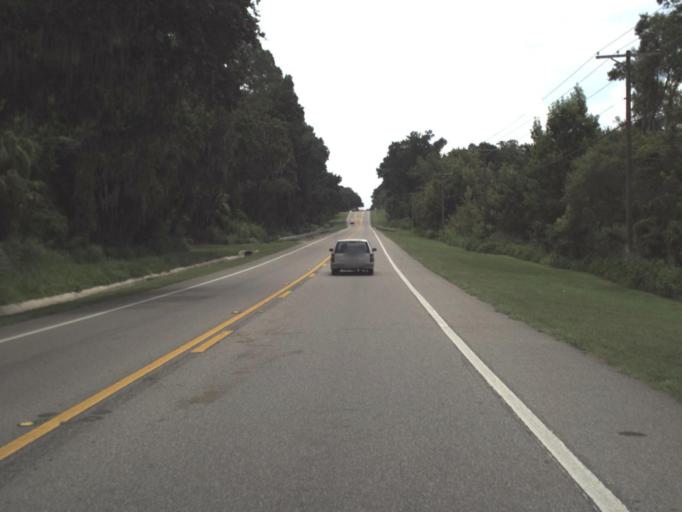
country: US
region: Florida
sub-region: Pasco County
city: Saint Leo
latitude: 28.3356
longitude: -82.2522
